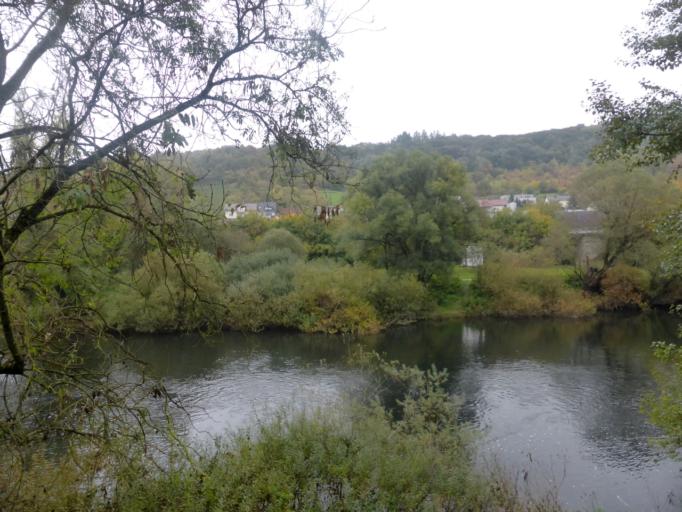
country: DE
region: Rheinland-Pfalz
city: Oberbillig
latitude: 49.7270
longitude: 6.5118
